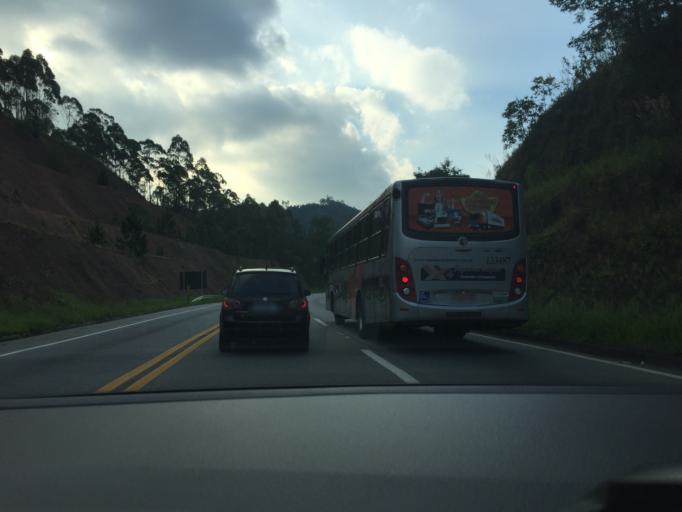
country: BR
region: Sao Paulo
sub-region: Francisco Morato
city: Francisco Morato
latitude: -23.2830
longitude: -46.8024
